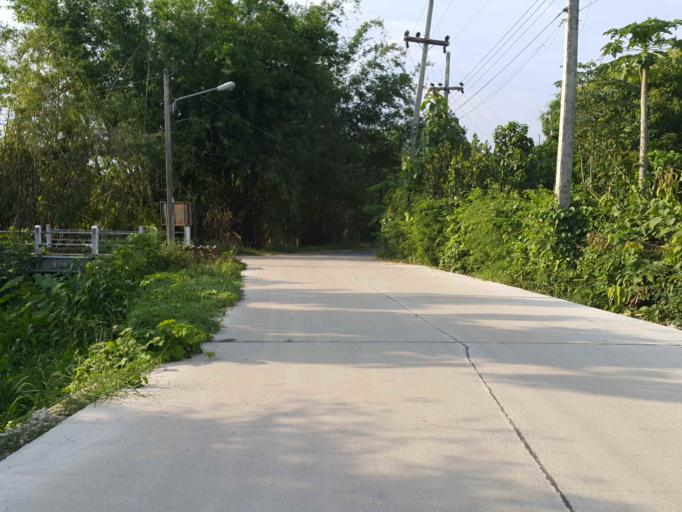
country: TH
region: Chiang Mai
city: San Sai
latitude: 18.8431
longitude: 99.0961
